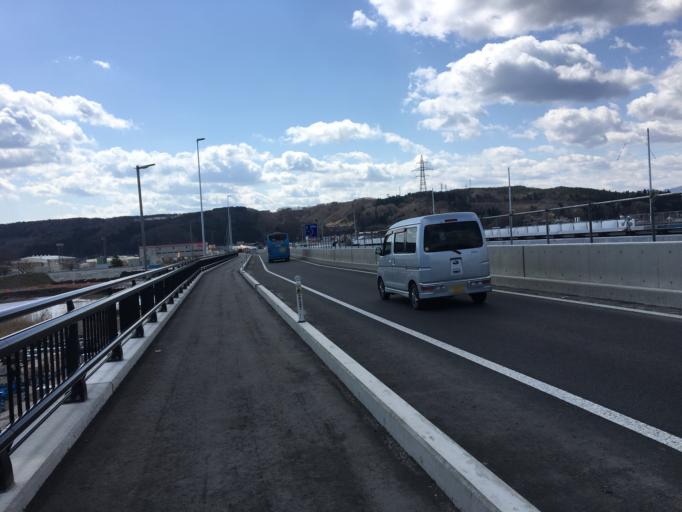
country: JP
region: Aomori
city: Hachinohe
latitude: 40.1949
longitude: 141.7842
